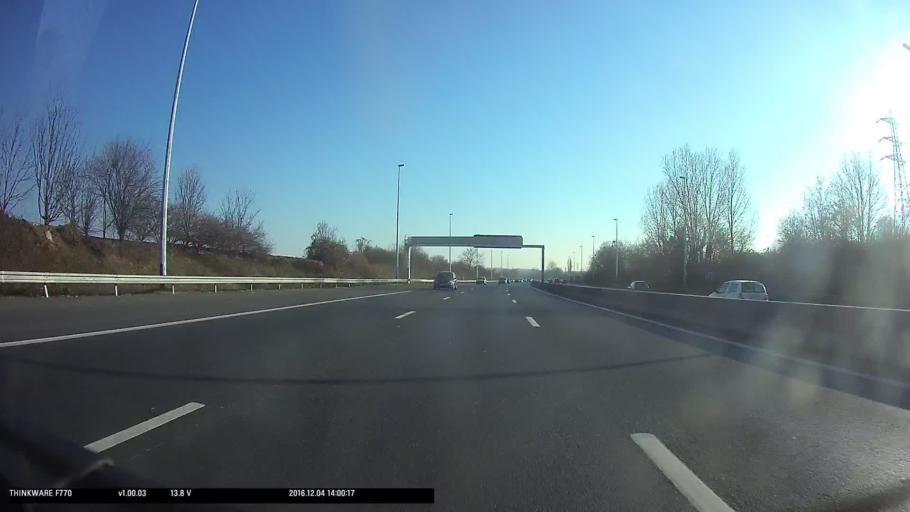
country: FR
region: Ile-de-France
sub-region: Departement du Val-d'Oise
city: Saint-Ouen-l'Aumone
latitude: 49.0280
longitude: 2.1291
